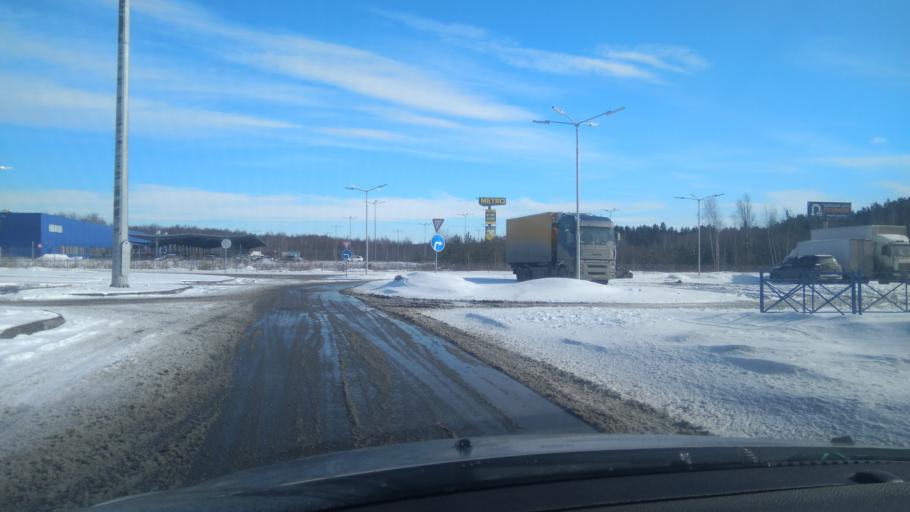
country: RU
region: Sverdlovsk
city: Istok
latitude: 56.8236
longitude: 60.7089
